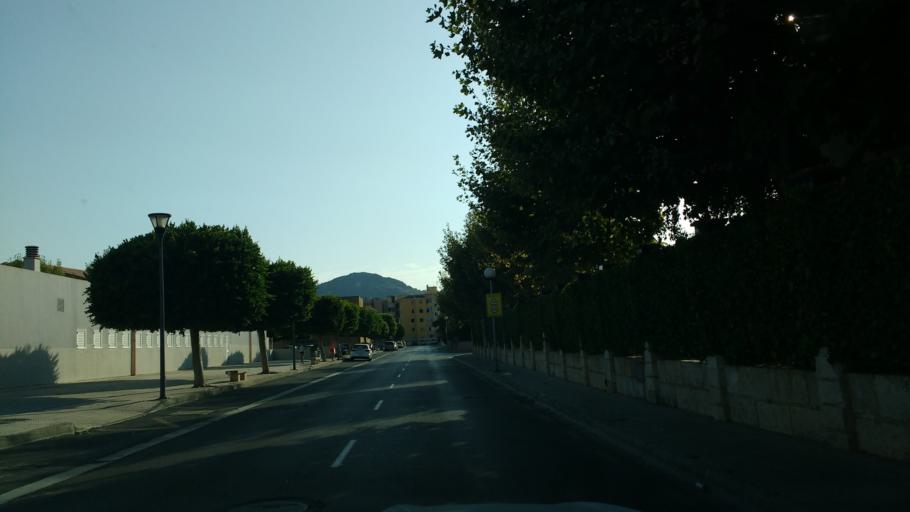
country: ES
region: Balearic Islands
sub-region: Illes Balears
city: Port d'Alcudia
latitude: 39.8415
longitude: 3.1250
